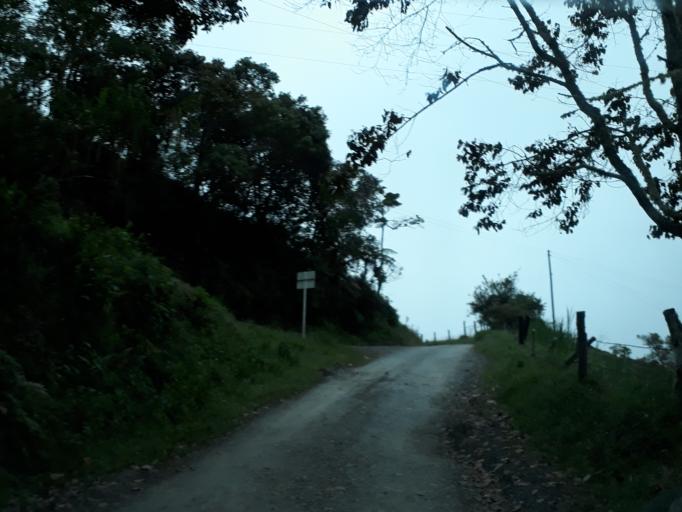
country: CO
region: Boyaca
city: Muzo
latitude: 5.3743
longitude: -74.0733
